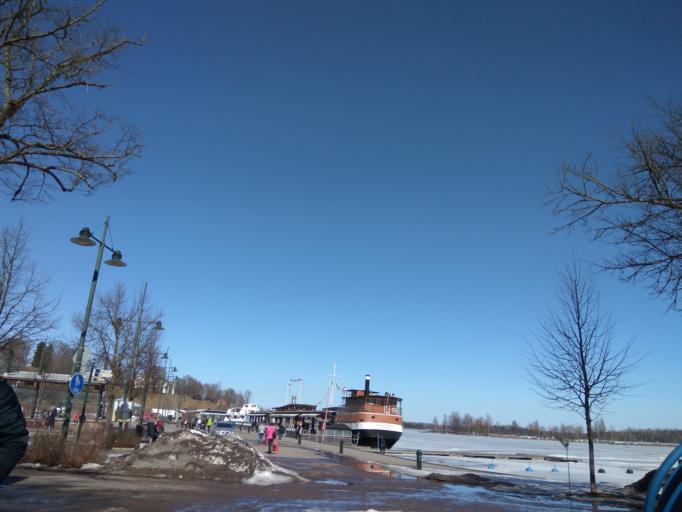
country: FI
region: South Karelia
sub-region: Lappeenranta
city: Lappeenranta
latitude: 61.0614
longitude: 28.1871
